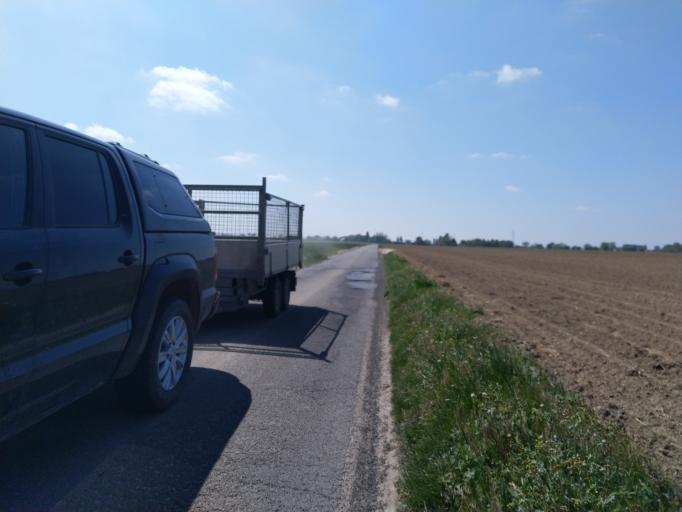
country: BE
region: Wallonia
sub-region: Province du Hainaut
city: Lens
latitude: 50.5430
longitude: 3.8575
